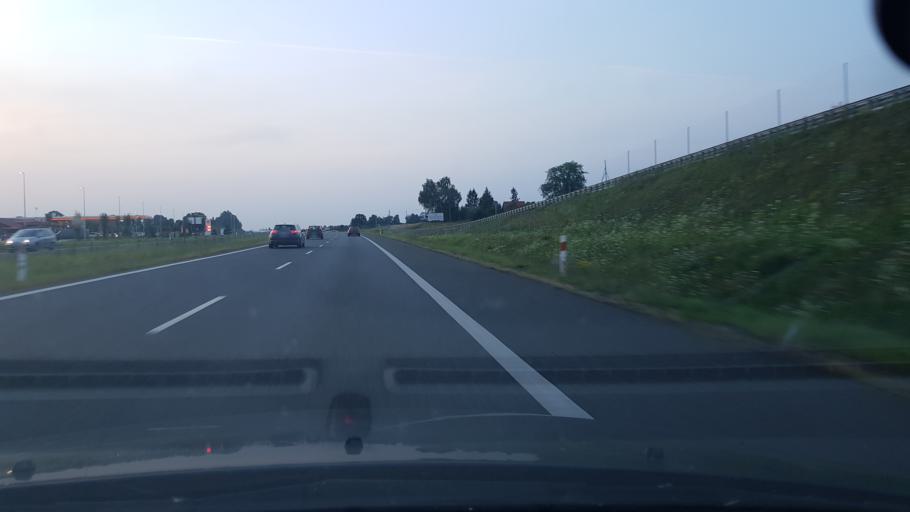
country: PL
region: Warmian-Masurian Voivodeship
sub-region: Powiat olsztynski
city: Olsztynek
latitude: 53.4788
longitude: 20.3214
